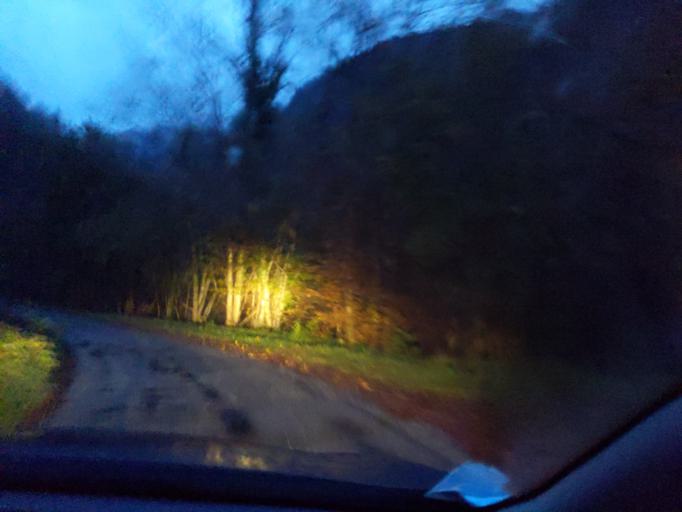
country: FR
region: Rhone-Alpes
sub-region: Departement de la Savoie
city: Aiton
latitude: 45.5196
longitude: 6.3401
